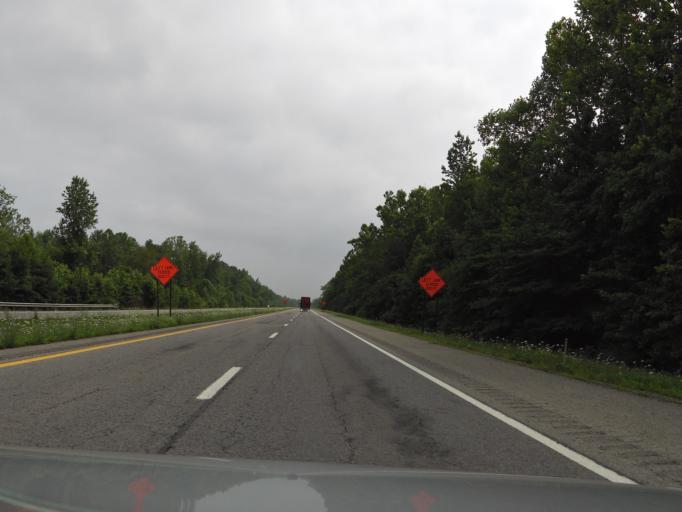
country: US
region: Kentucky
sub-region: Muhlenberg County
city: Morehead
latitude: 37.2639
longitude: -87.1673
